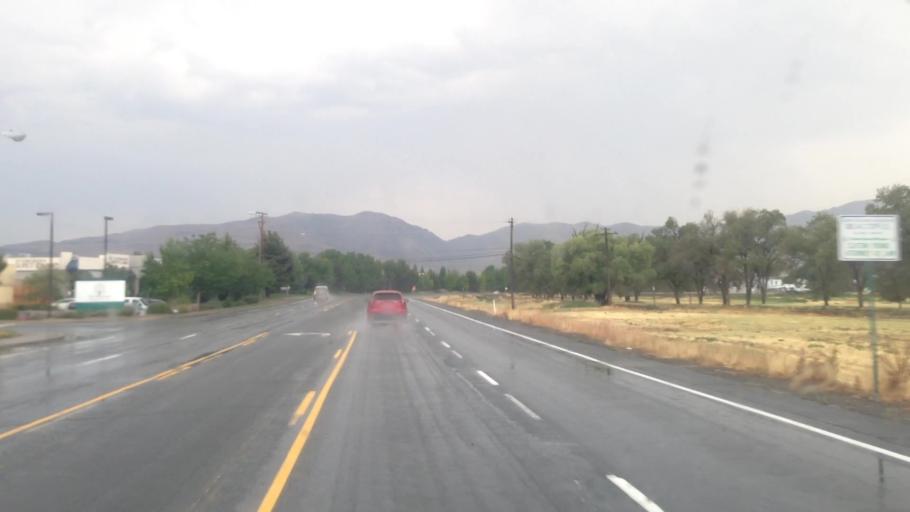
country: US
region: Nevada
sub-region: Washoe County
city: Sparks
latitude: 39.5009
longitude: -119.7588
